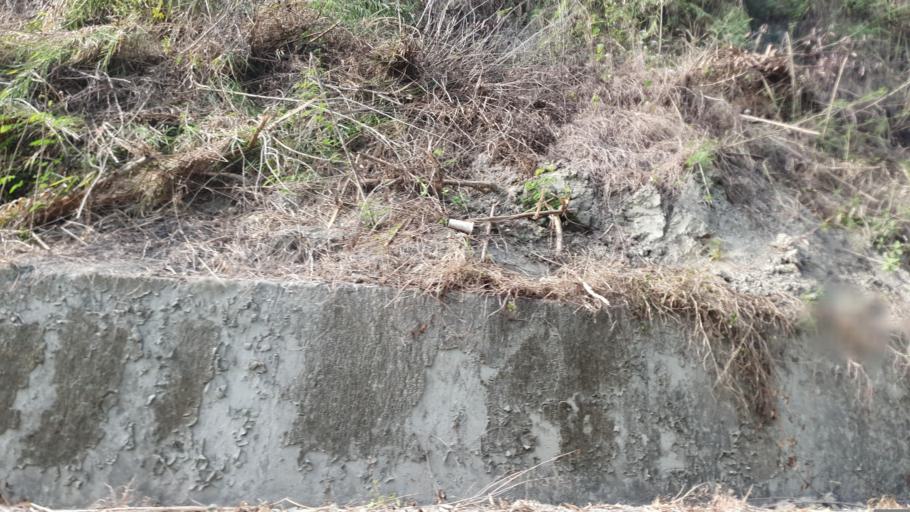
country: TW
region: Taiwan
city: Yujing
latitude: 23.0315
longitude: 120.3935
